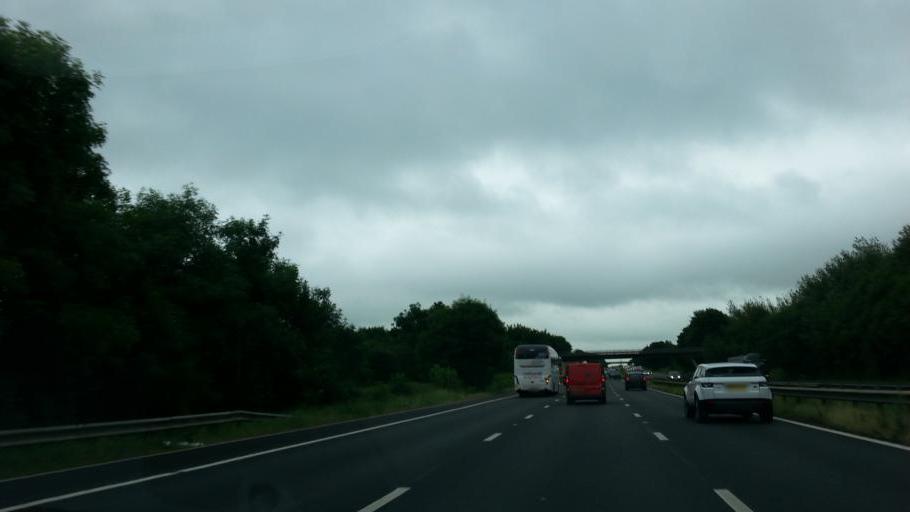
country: GB
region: England
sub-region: Leicestershire
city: Cosby
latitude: 52.5138
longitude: -1.1802
